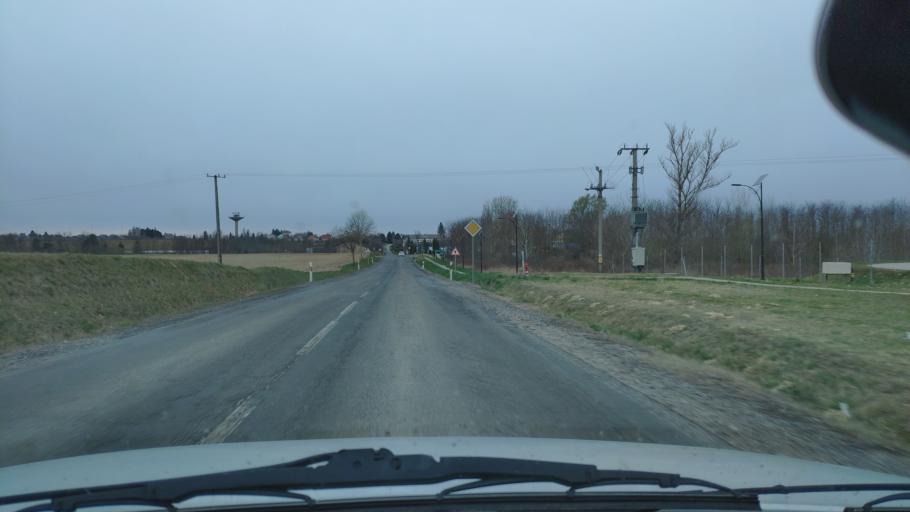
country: HU
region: Zala
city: Pacsa
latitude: 46.7244
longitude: 17.0286
